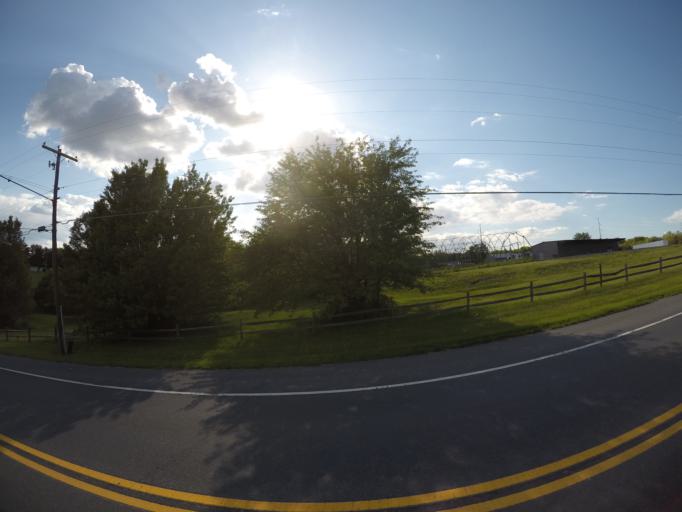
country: US
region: Maryland
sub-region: Montgomery County
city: Damascus
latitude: 39.3202
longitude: -77.1958
